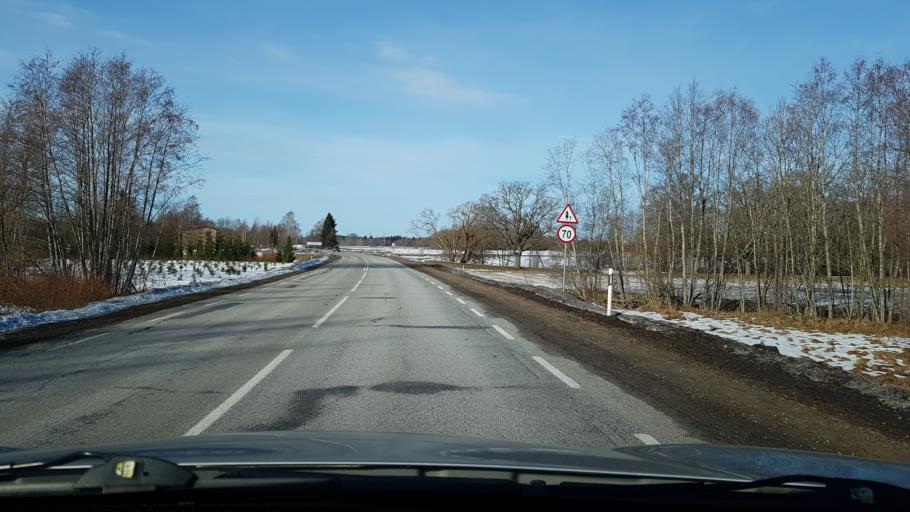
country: EE
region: Viljandimaa
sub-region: Suure-Jaani vald
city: Suure-Jaani
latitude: 58.5429
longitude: 25.4799
